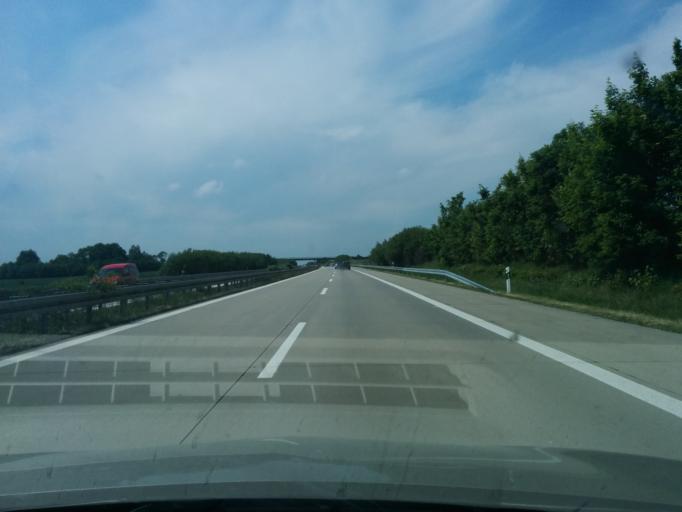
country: DE
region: Mecklenburg-Vorpommern
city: Gross Miltzow
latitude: 53.5519
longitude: 13.6623
